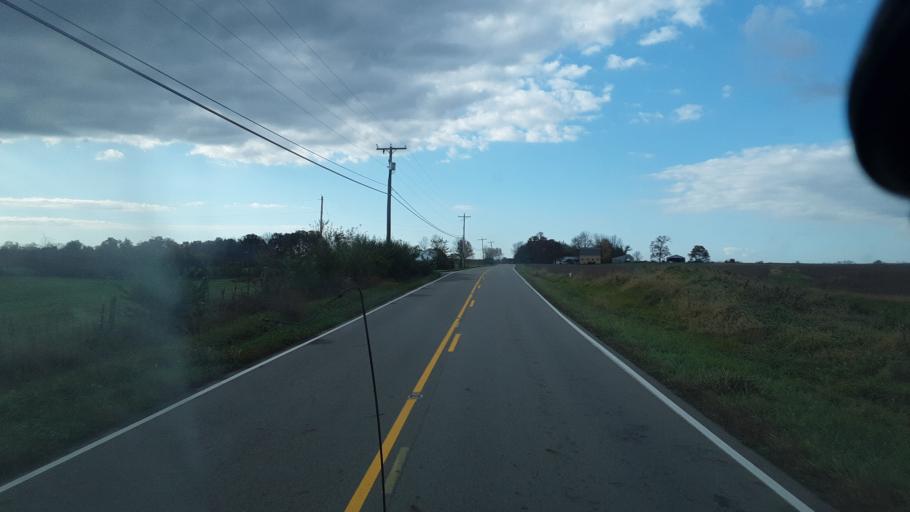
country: US
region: Ohio
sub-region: Highland County
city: Leesburg
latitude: 39.3816
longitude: -83.4694
